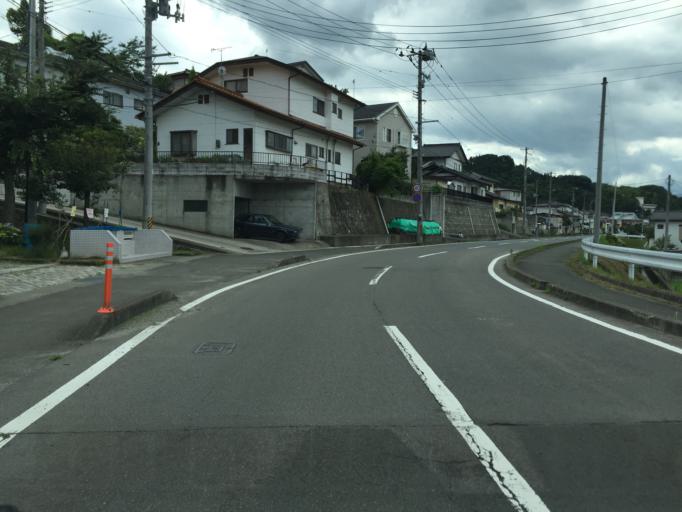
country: JP
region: Fukushima
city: Fukushima-shi
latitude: 37.7433
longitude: 140.4853
